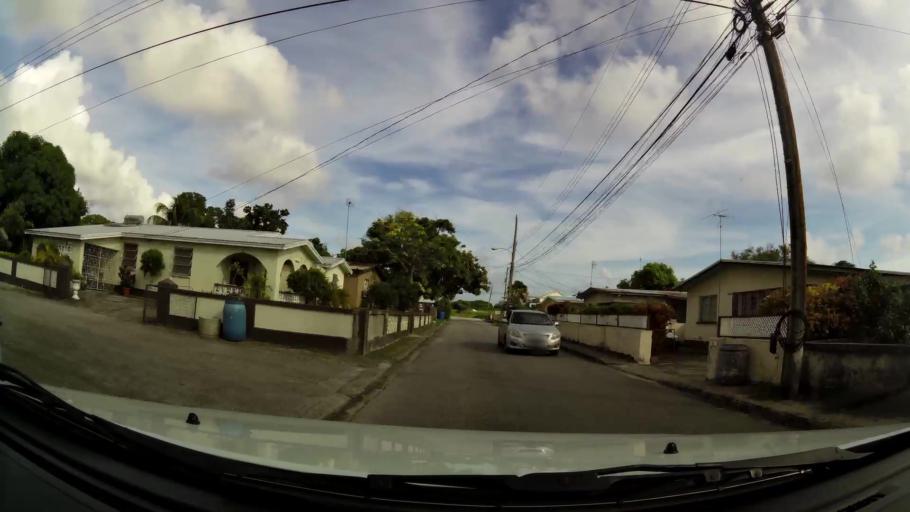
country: BB
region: Saint Michael
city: Bridgetown
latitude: 13.0826
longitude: -59.5797
